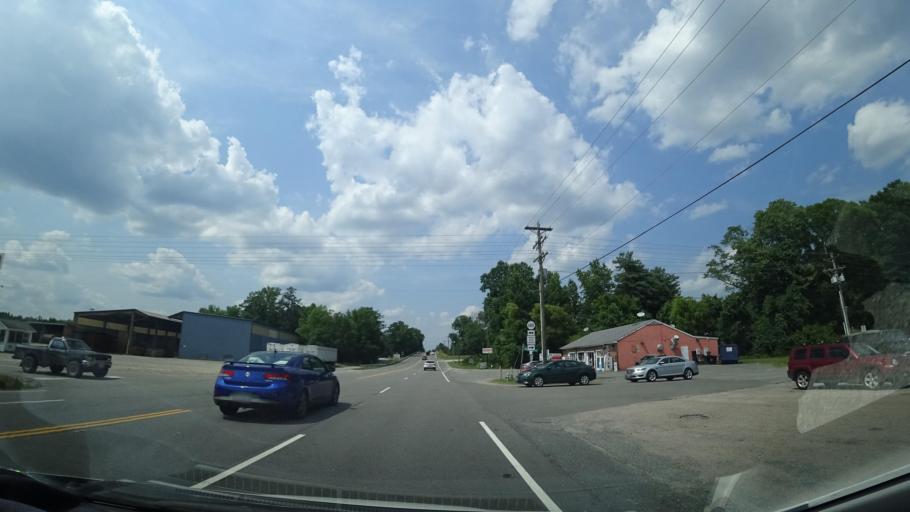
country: US
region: Virginia
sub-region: Hanover County
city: Ashland
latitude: 37.8601
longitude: -77.4642
